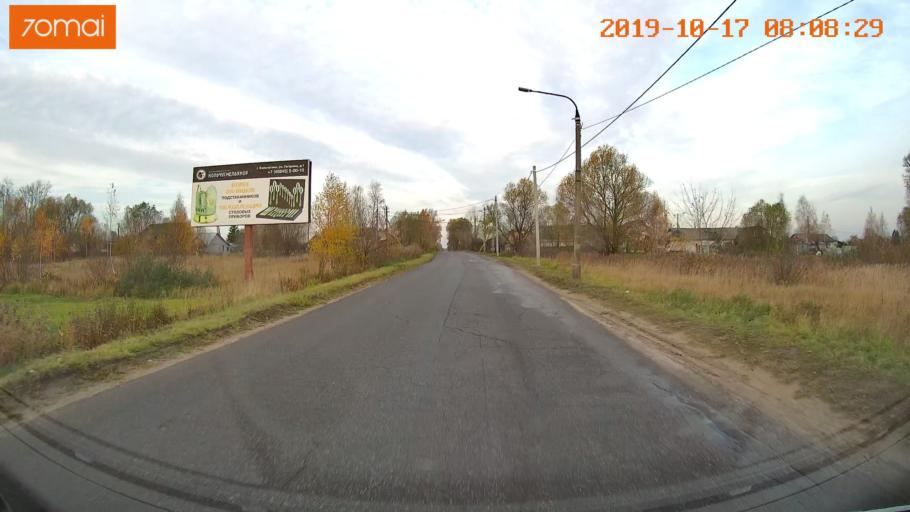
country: RU
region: Vladimir
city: Kol'chugino
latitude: 56.3143
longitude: 39.3877
